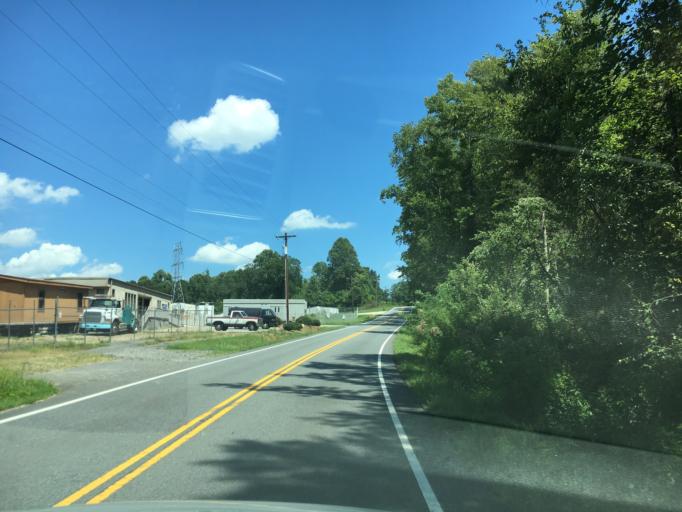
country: US
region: South Carolina
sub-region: Spartanburg County
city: Wellford
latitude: 34.8918
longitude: -82.0998
